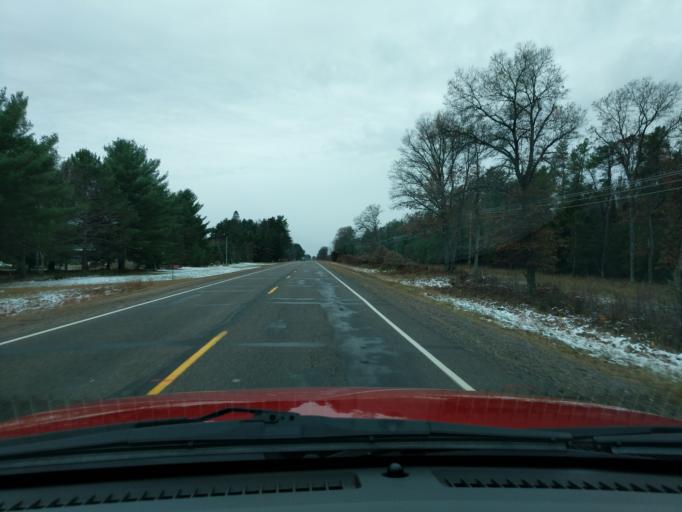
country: US
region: Wisconsin
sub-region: Burnett County
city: Siren
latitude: 45.8167
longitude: -92.3469
